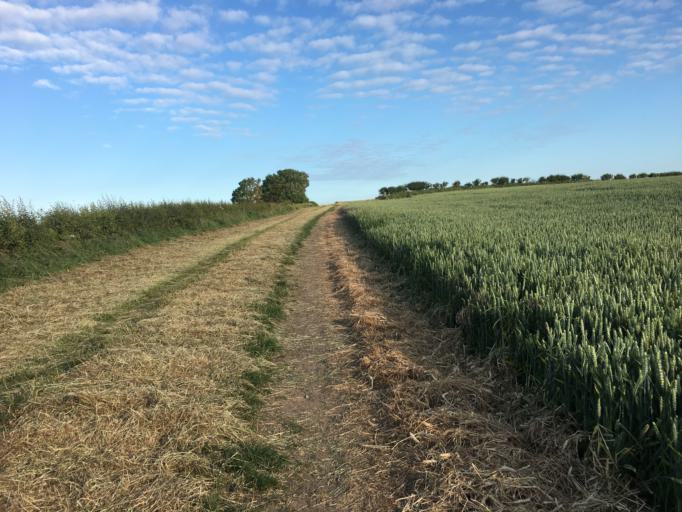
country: GB
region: England
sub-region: Northumberland
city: Bamburgh
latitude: 55.6008
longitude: -1.6984
